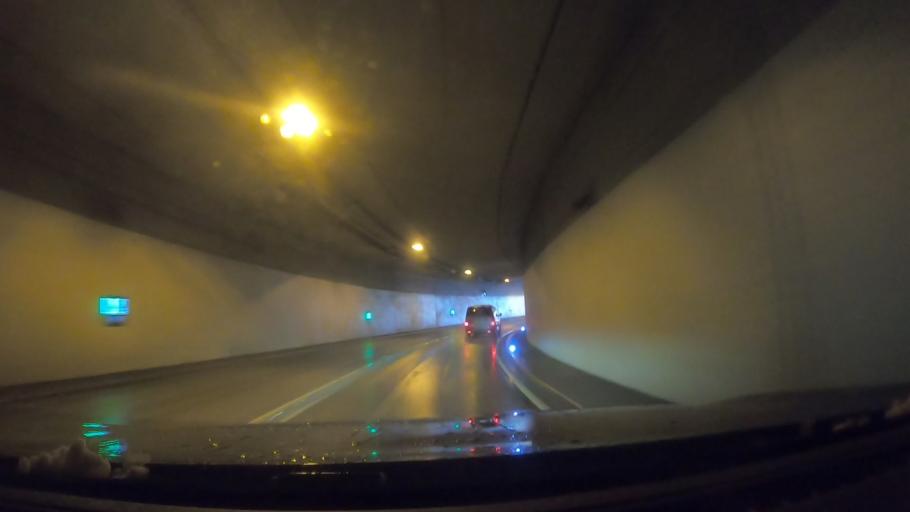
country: DE
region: Bavaria
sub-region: Upper Bavaria
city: Ruhpolding
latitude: 47.7649
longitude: 12.6480
